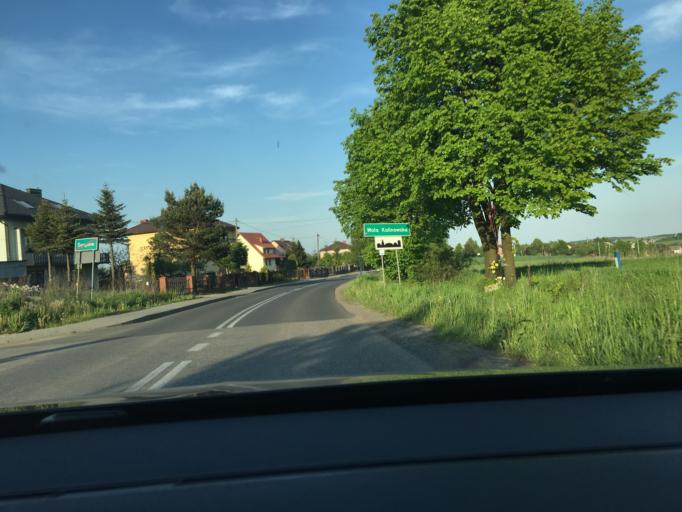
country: PL
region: Lesser Poland Voivodeship
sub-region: Powiat krakowski
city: Saspow
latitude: 50.2311
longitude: 19.7815
